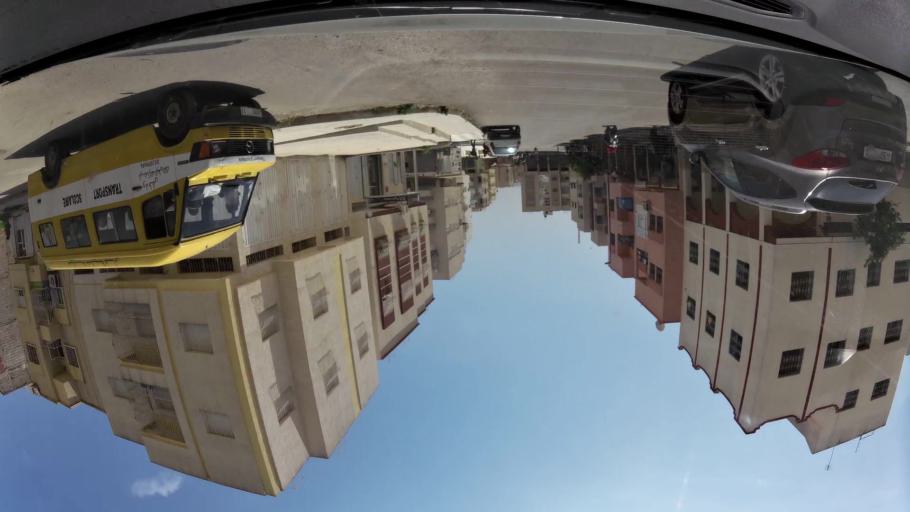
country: MA
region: Fes-Boulemane
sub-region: Fes
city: Fes
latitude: 34.0615
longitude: -5.0205
